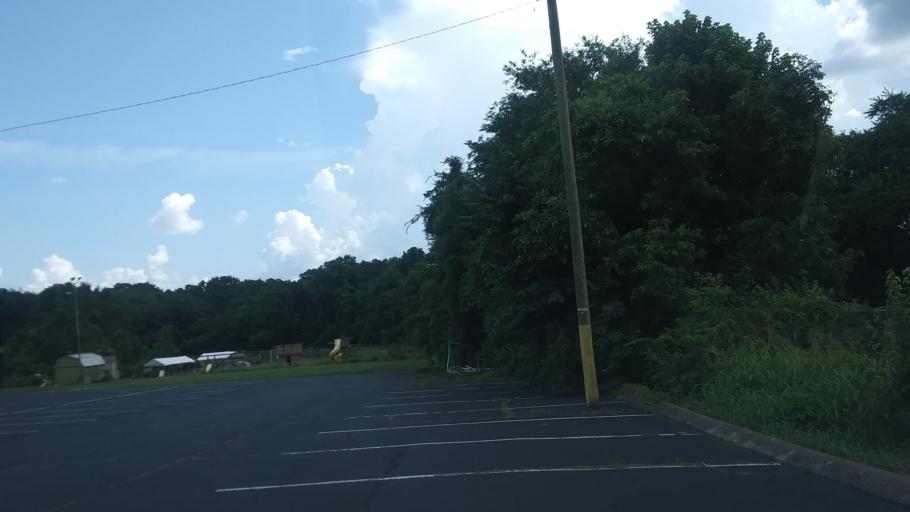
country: US
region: Tennessee
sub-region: Davidson County
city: Oak Hill
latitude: 36.0673
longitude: -86.7074
